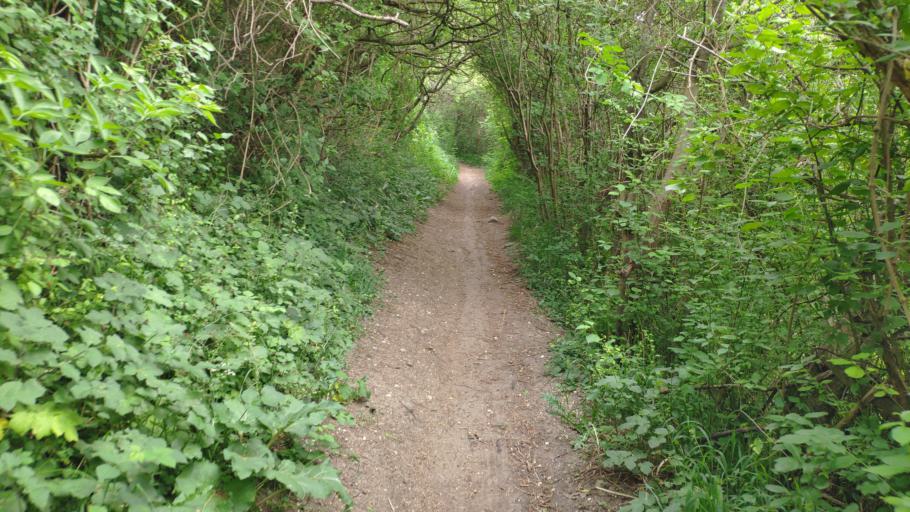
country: NL
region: Limburg
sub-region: Gemeente Vaals
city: Vaals
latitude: 50.7861
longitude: 6.0121
